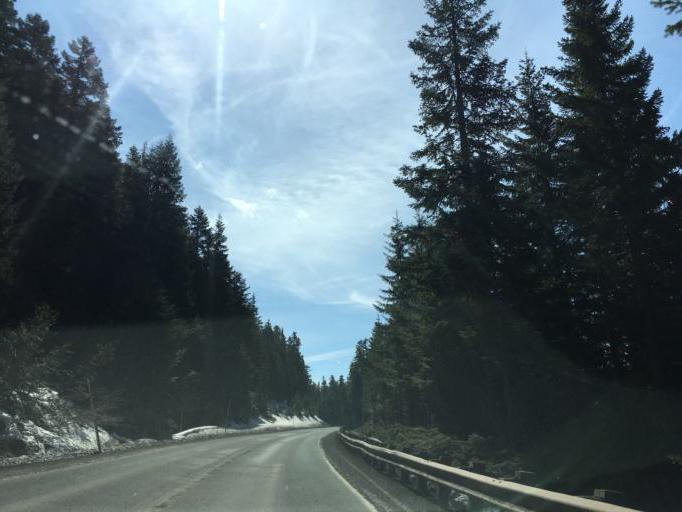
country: US
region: Oregon
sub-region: Clackamas County
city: Mount Hood Village
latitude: 45.3049
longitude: -121.7303
